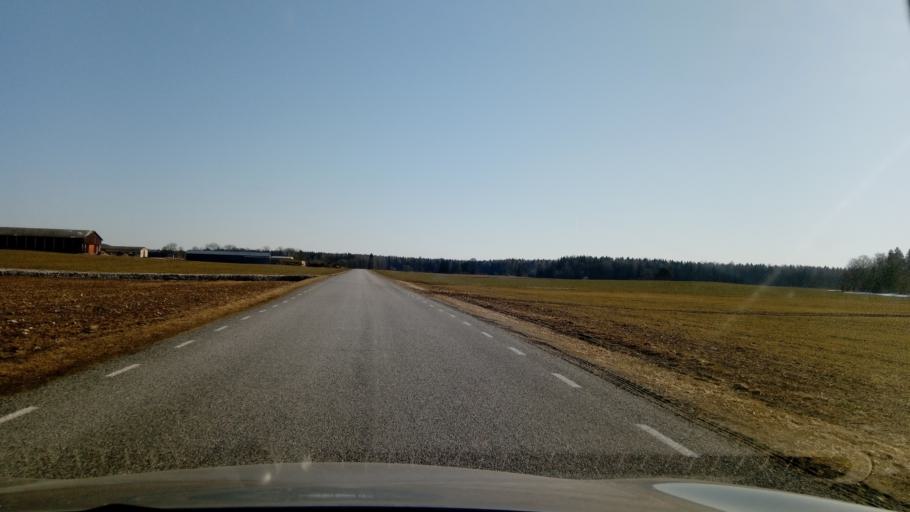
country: EE
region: Laeaene-Virumaa
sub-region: Kadrina vald
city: Kadrina
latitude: 59.2459
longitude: 26.2054
